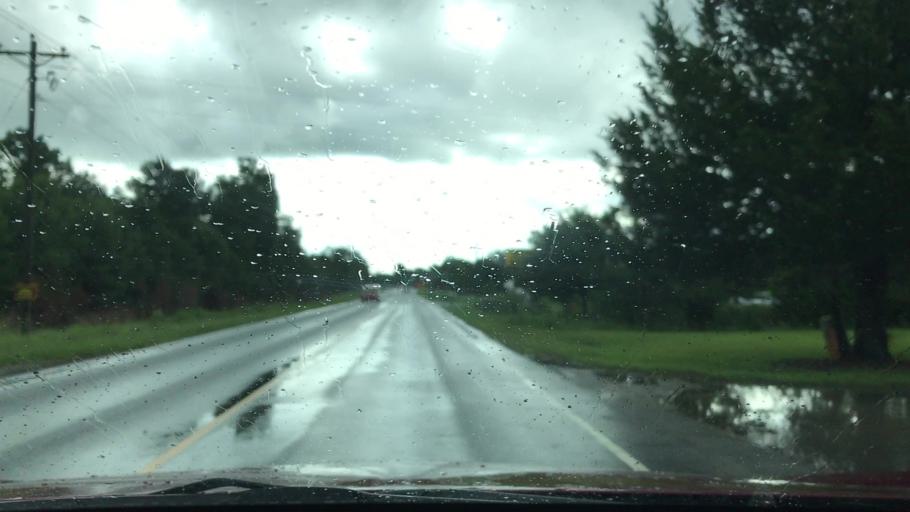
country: US
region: South Carolina
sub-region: Horry County
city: Loris
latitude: 33.9051
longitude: -78.8453
